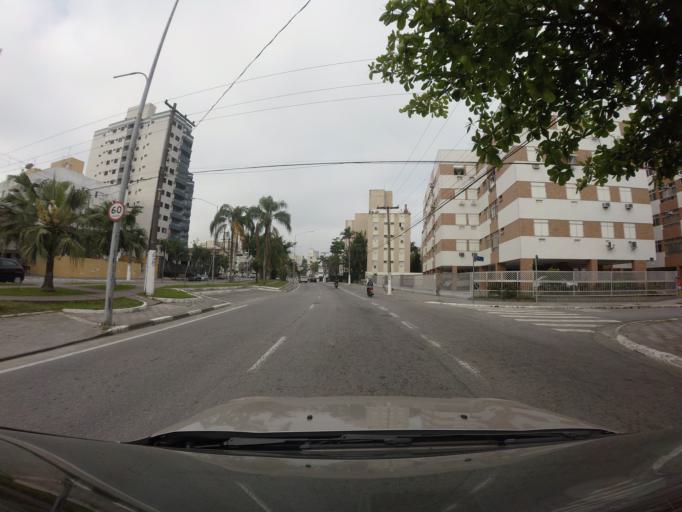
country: BR
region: Sao Paulo
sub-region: Guaruja
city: Guaruja
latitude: -23.9875
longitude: -46.2447
